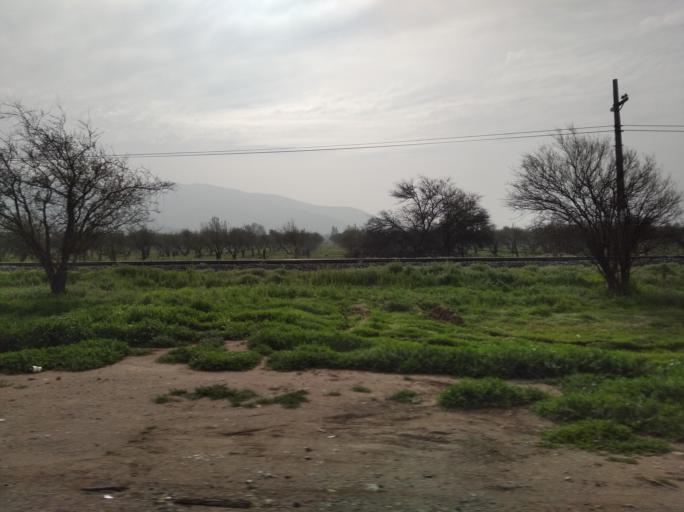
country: CL
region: Santiago Metropolitan
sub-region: Provincia de Chacabuco
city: Lampa
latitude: -33.1566
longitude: -70.8996
